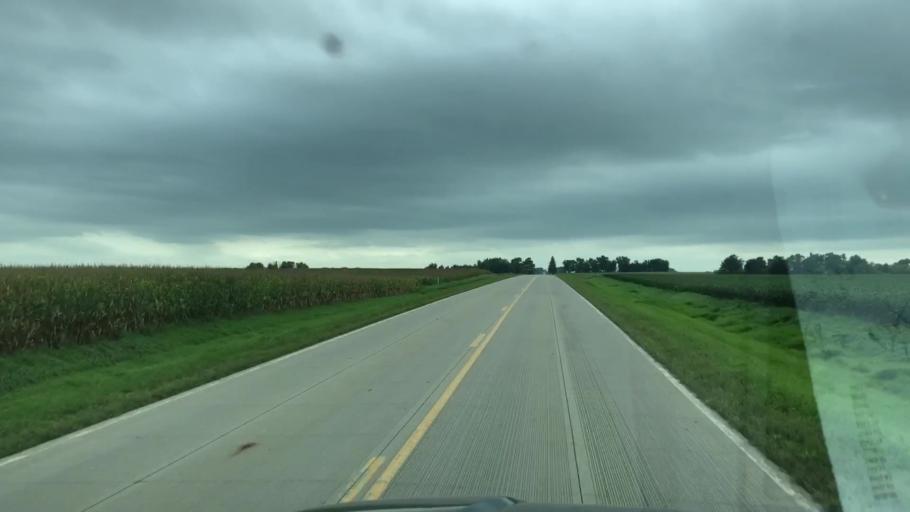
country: US
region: Iowa
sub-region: Sioux County
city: Alton
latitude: 43.1179
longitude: -95.9788
